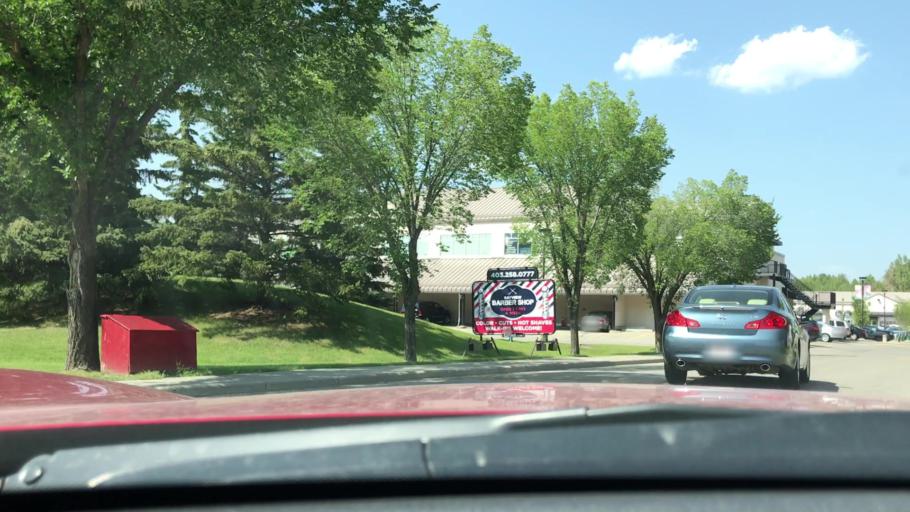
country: CA
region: Alberta
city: Calgary
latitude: 50.9724
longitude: -114.0979
